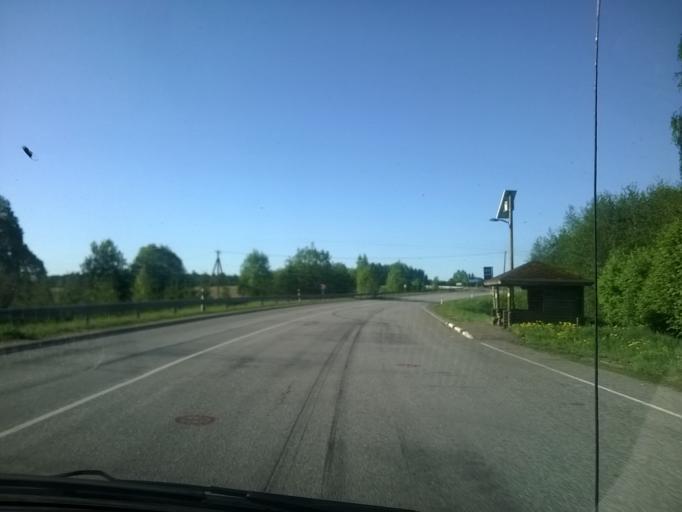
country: EE
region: Valgamaa
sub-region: Valga linn
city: Valga
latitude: 57.9090
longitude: 26.1832
